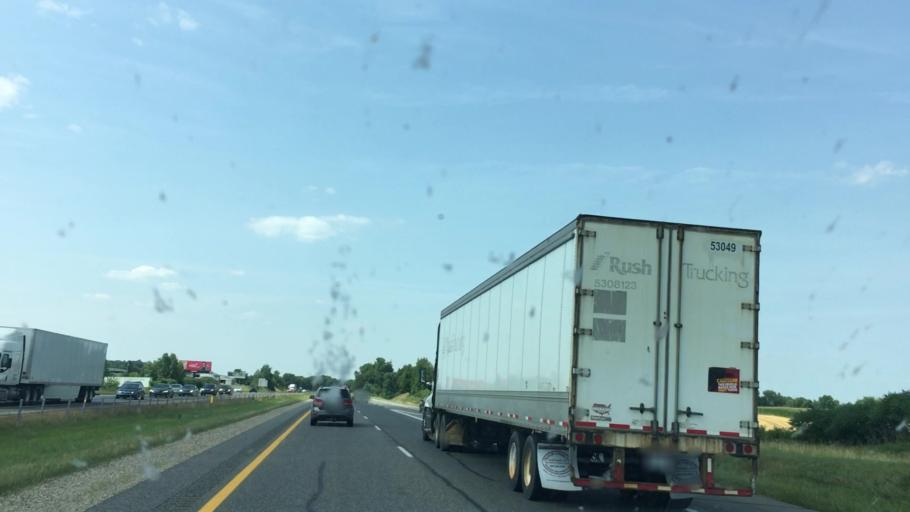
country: US
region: Michigan
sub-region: Allegan County
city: Otsego
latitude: 42.5386
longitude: -85.6603
